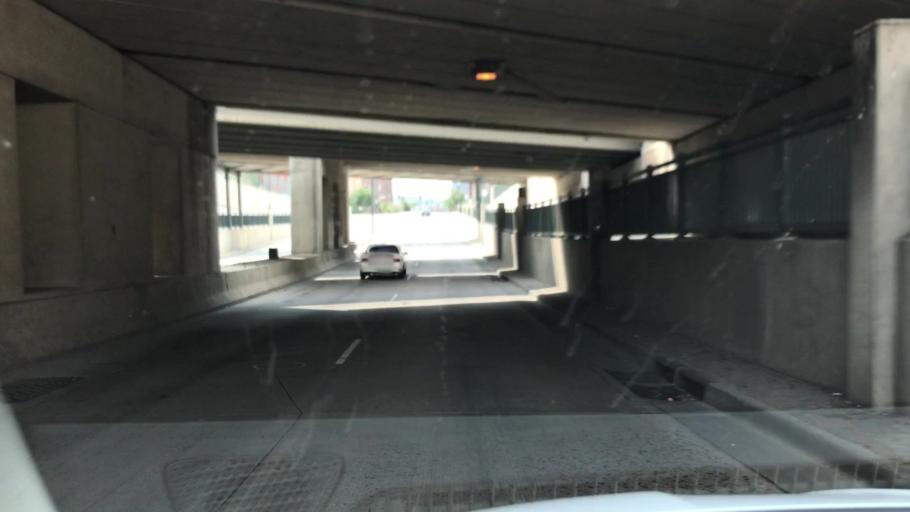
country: US
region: Colorado
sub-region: Denver County
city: Denver
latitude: 39.7617
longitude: -104.9882
